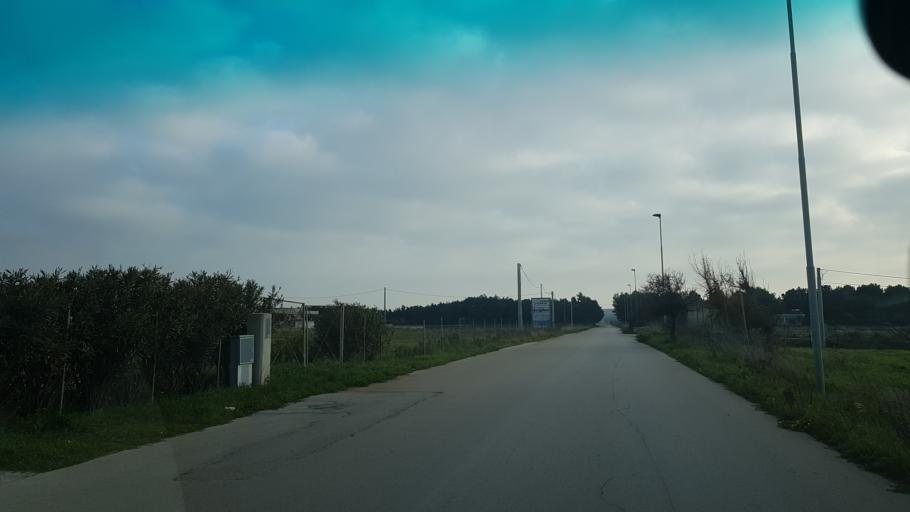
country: IT
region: Apulia
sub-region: Provincia di Brindisi
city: Carovigno
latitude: 40.7434
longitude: 17.7294
